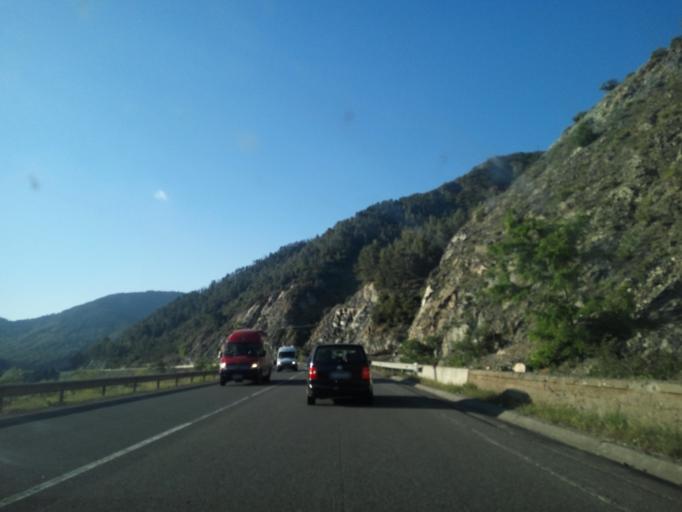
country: AL
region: Lezhe
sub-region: Rrethi i Mirdites
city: Rubik
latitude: 41.7726
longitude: 19.7897
